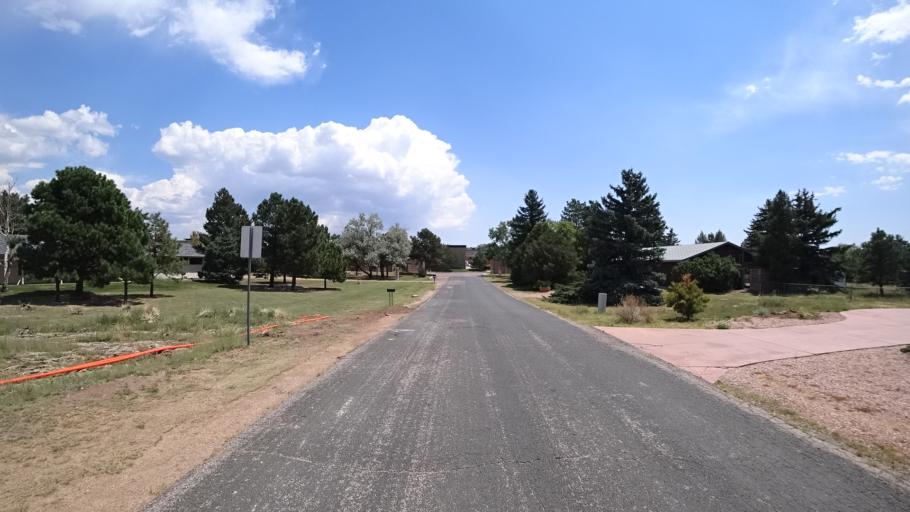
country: US
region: Colorado
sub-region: El Paso County
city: Air Force Academy
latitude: 38.9384
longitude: -104.8009
